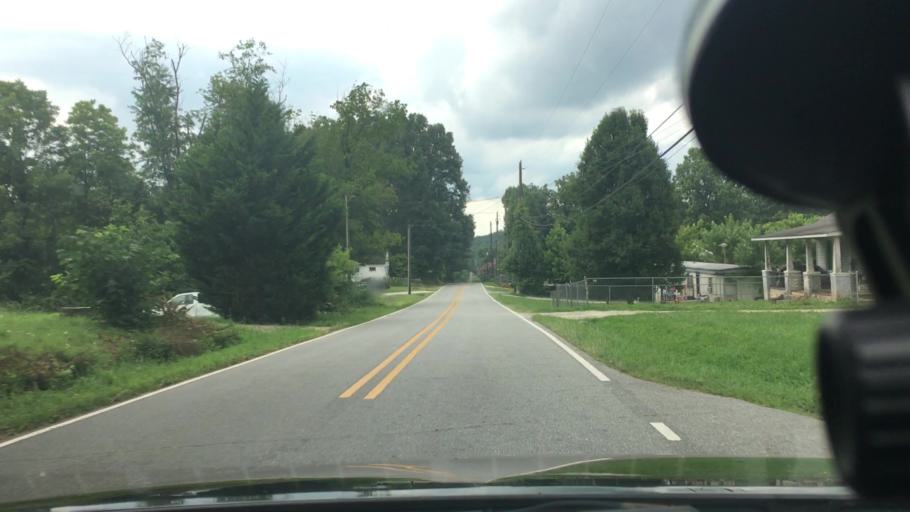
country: US
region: North Carolina
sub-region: McDowell County
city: West Marion
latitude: 35.6649
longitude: -82.0175
